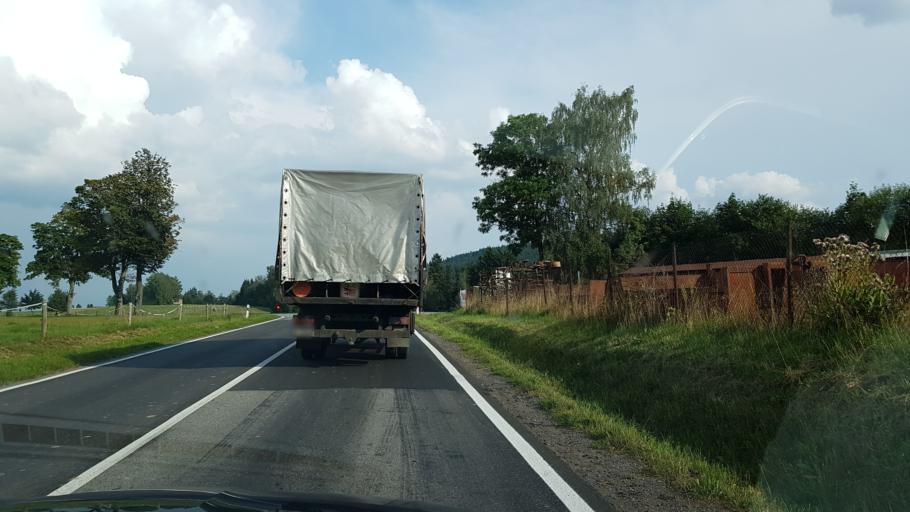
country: PL
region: Lower Silesian Voivodeship
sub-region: Powiat klodzki
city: Miedzylesie
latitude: 50.0987
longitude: 16.6362
